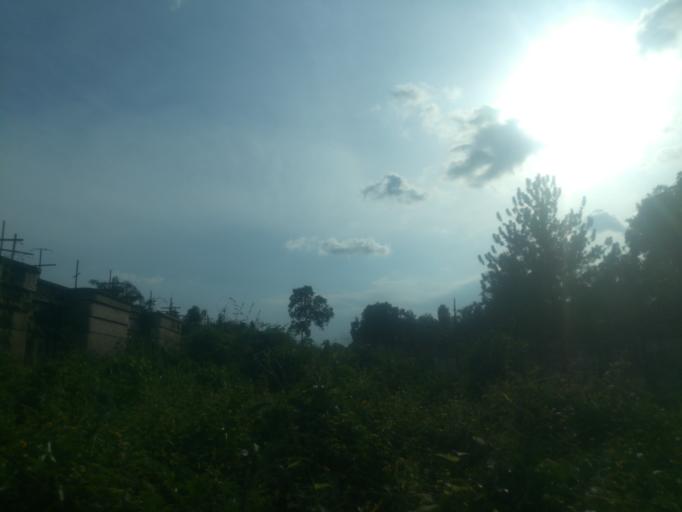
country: NG
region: Oyo
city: Ibadan
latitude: 7.3808
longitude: 3.8707
